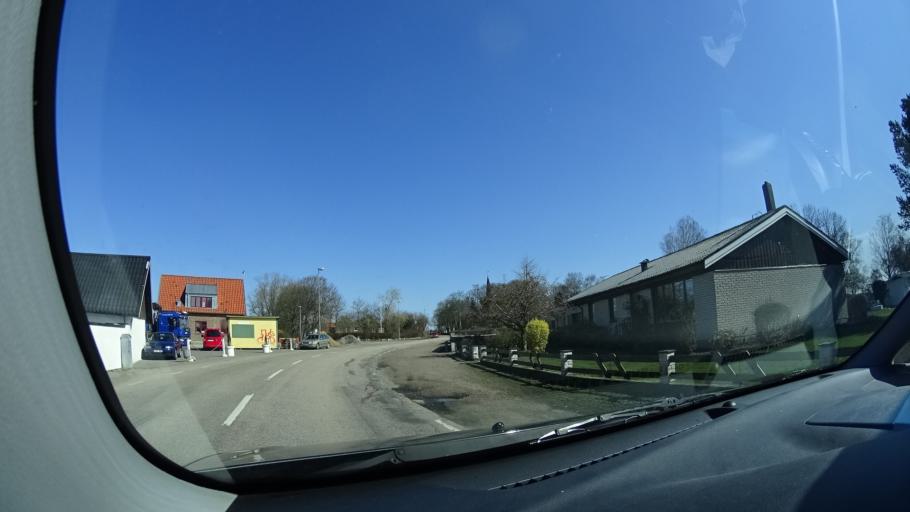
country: SE
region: Skane
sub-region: Hoganas Kommun
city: Hoganas
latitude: 56.2054
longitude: 12.5922
